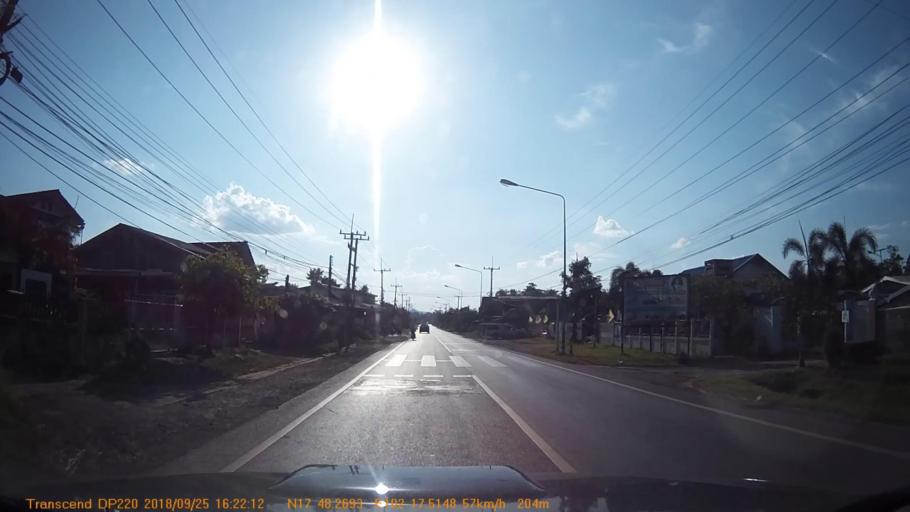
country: TH
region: Changwat Udon Thani
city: Nam Som
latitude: 17.8045
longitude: 102.2920
